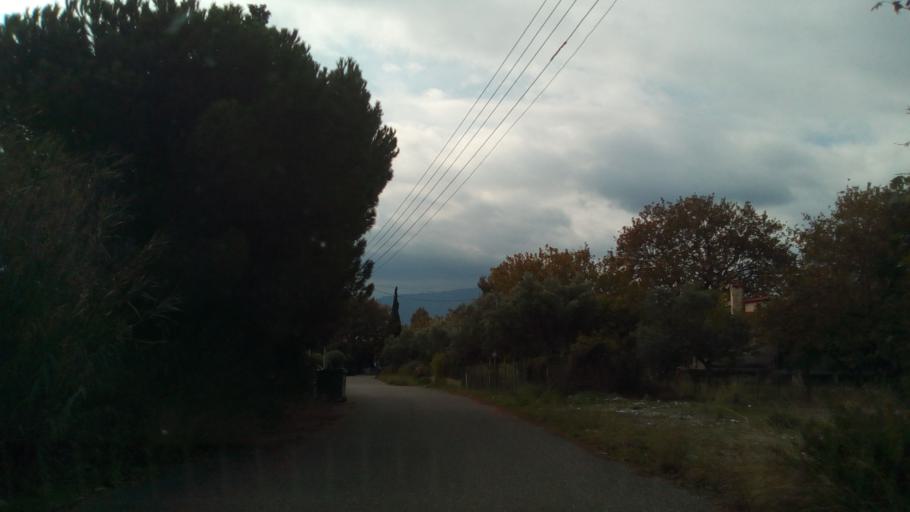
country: GR
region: West Greece
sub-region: Nomos Achaias
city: Kamarai
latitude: 38.3930
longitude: 22.0016
